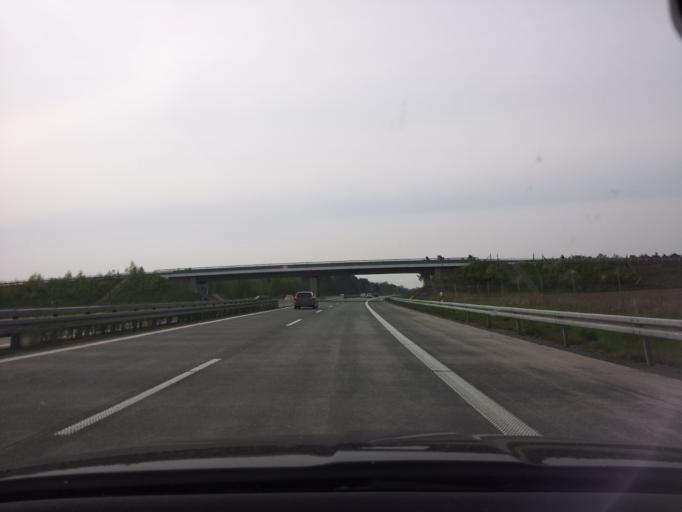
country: DE
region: Brandenburg
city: Lubbenau
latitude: 51.8702
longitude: 13.8968
